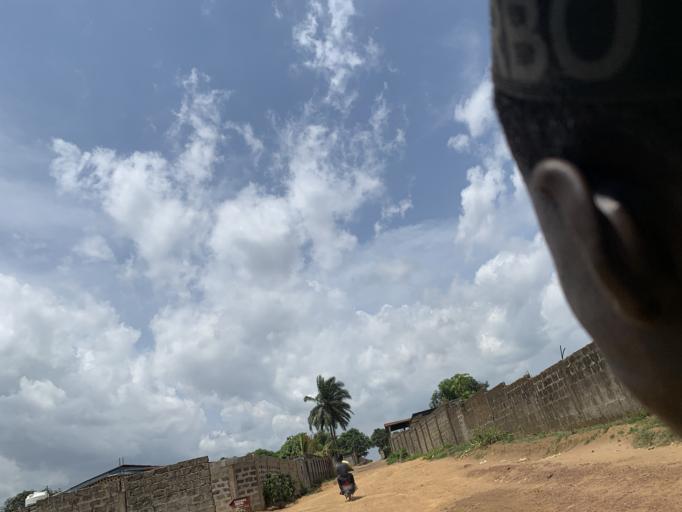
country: SL
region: Western Area
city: Waterloo
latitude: 8.3366
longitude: -13.0332
